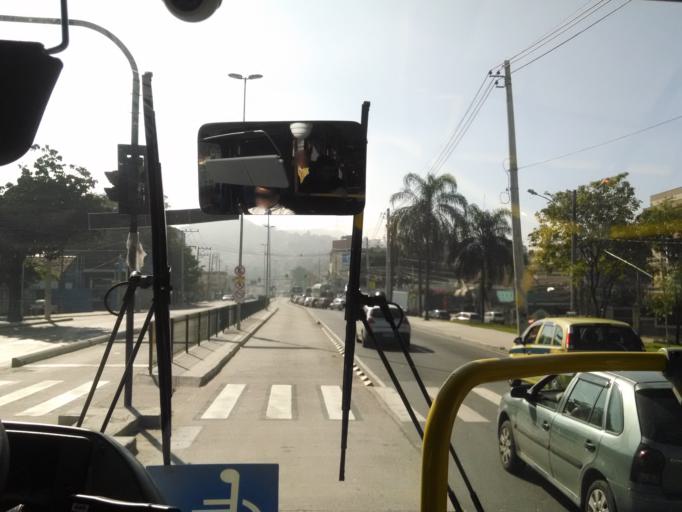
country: BR
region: Rio de Janeiro
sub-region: Sao Joao De Meriti
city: Sao Joao de Meriti
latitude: -22.9186
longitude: -43.3653
